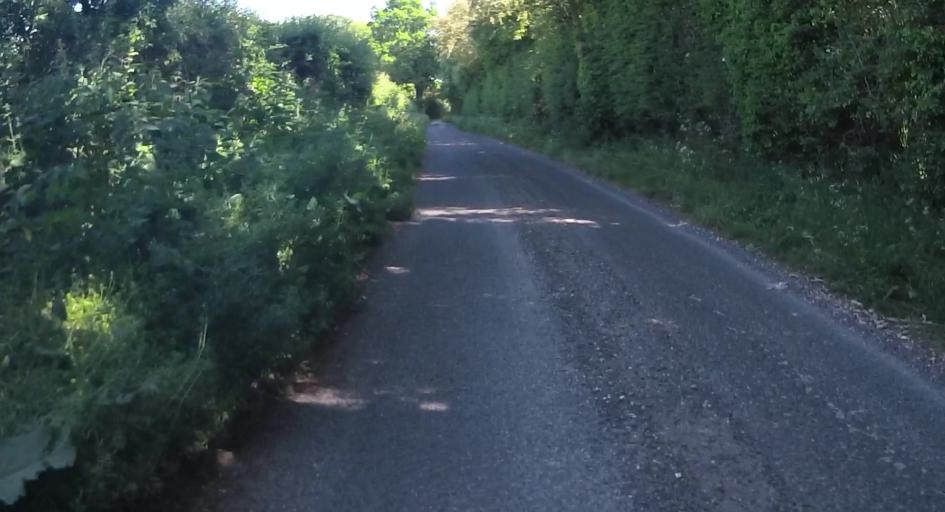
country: GB
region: England
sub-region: Hampshire
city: Overton
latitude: 51.2820
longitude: -1.2621
